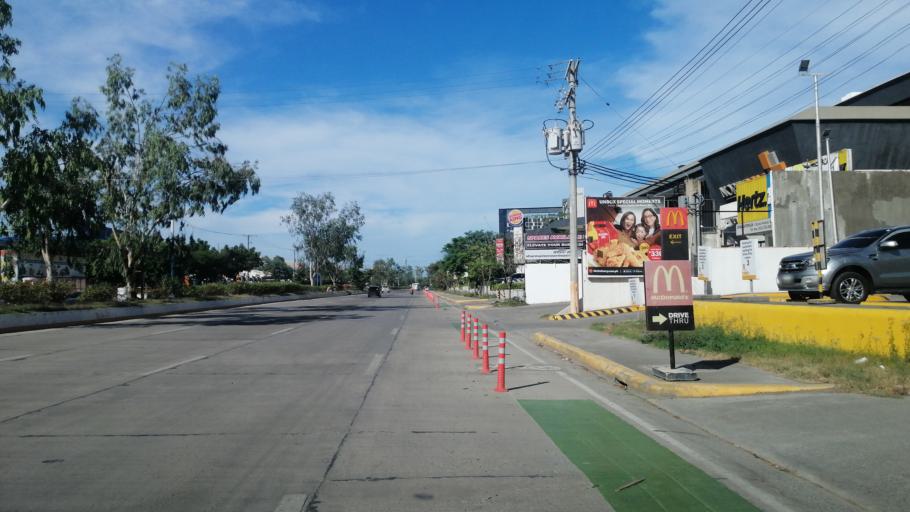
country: PH
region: Central Visayas
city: Mandaue City
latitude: 10.3216
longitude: 123.9328
